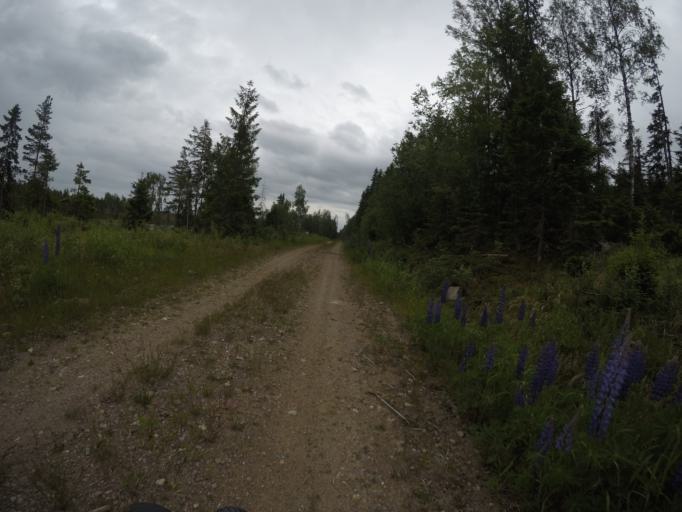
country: SE
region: Dalarna
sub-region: Ludvika Kommun
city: Abborrberget
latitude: 60.0348
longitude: 14.5981
